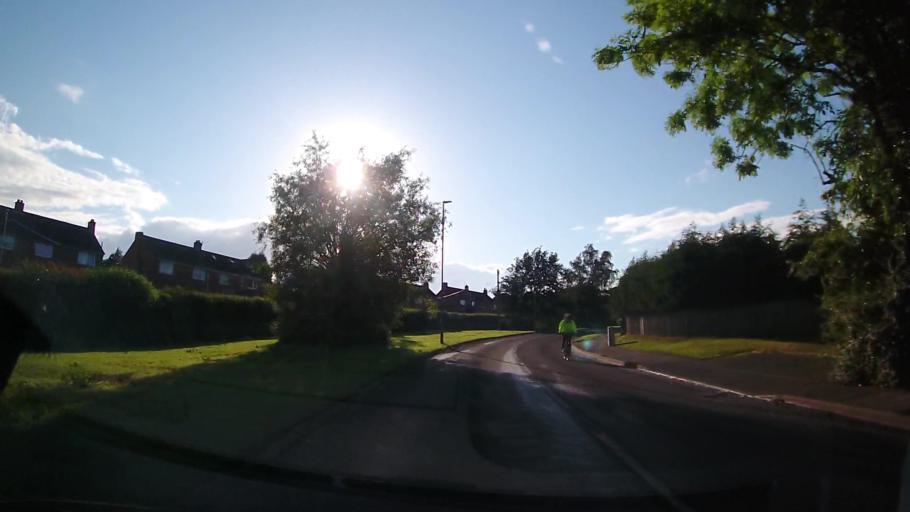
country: GB
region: England
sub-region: Leicestershire
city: Kirby Muxloe
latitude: 52.6531
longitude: -1.2456
